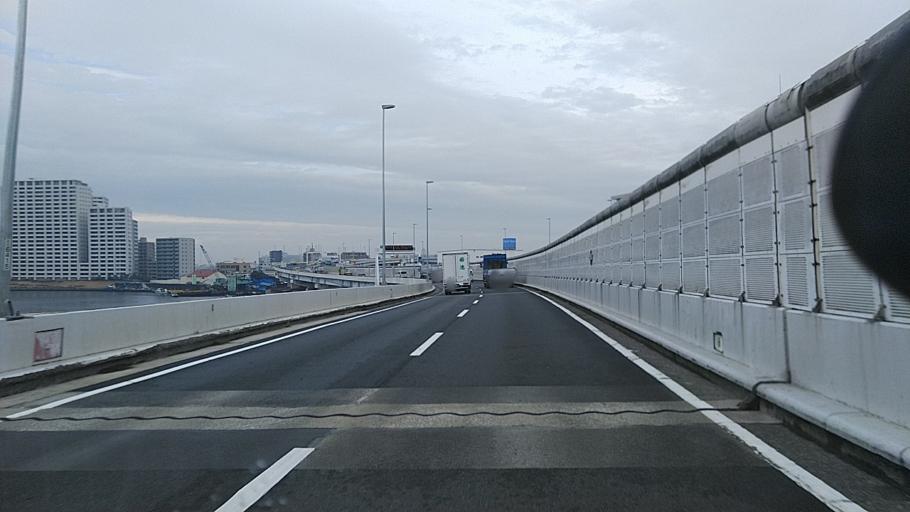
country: JP
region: Saitama
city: Soka
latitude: 35.7364
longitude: 139.8169
